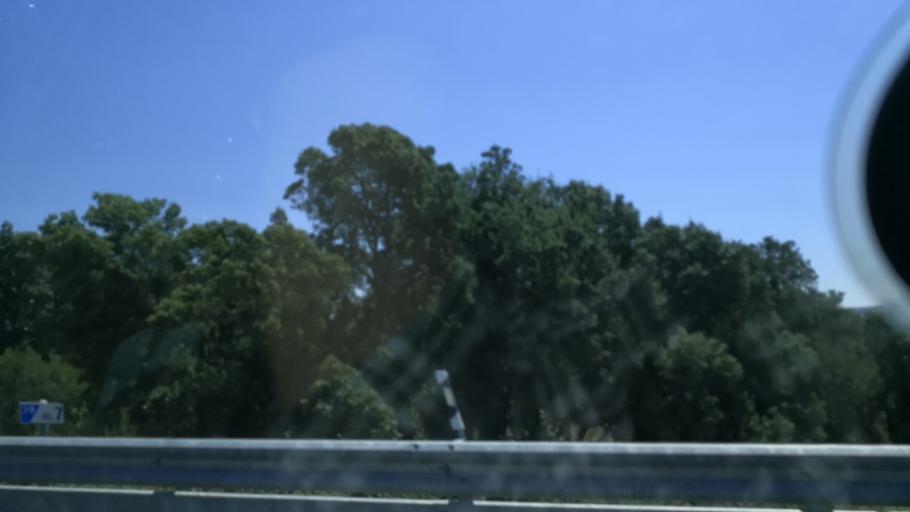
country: PT
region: Braganca
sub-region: Braganca Municipality
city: Braganca
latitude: 41.6979
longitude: -6.8104
